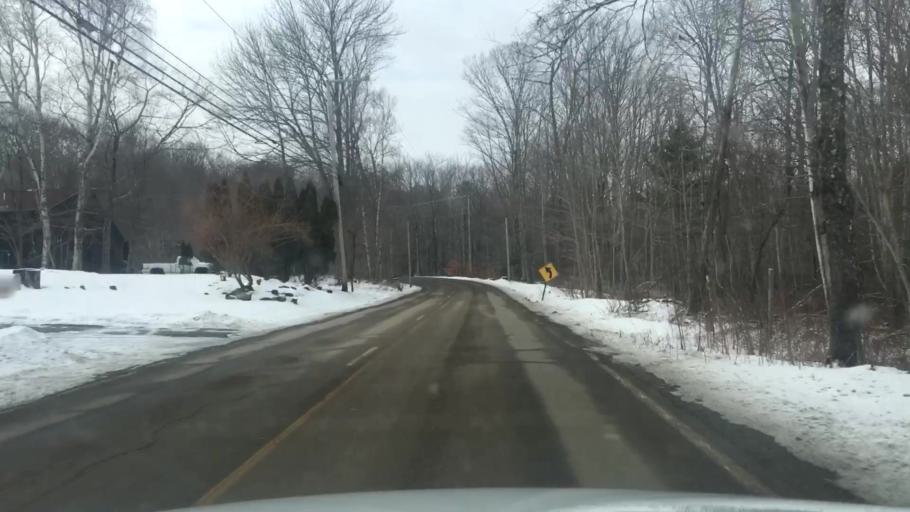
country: US
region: Maine
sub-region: Waldo County
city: Lincolnville
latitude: 44.2911
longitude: -69.0717
